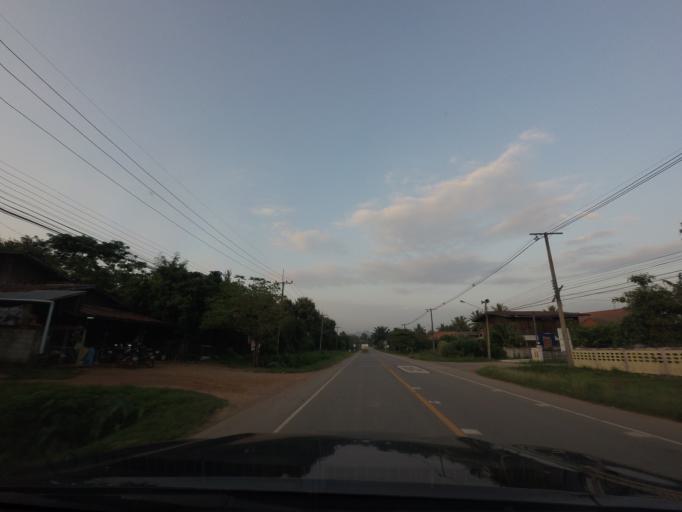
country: TH
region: Nan
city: Na Noi
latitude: 18.3507
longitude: 100.7155
